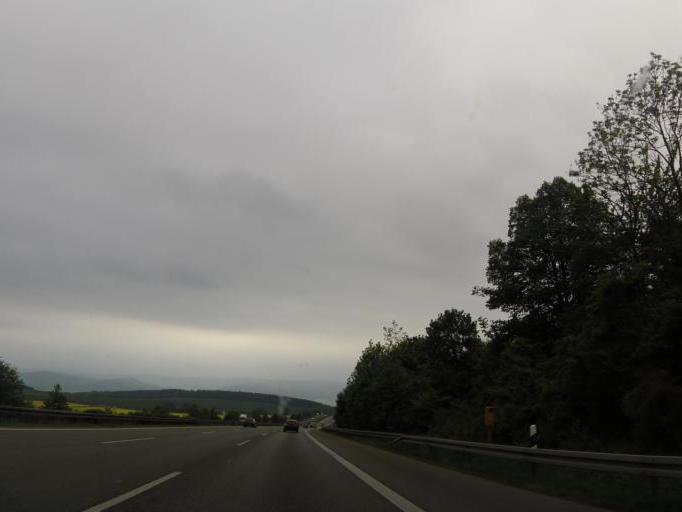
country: DE
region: Lower Saxony
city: Juhnde
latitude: 51.4088
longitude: 9.8226
